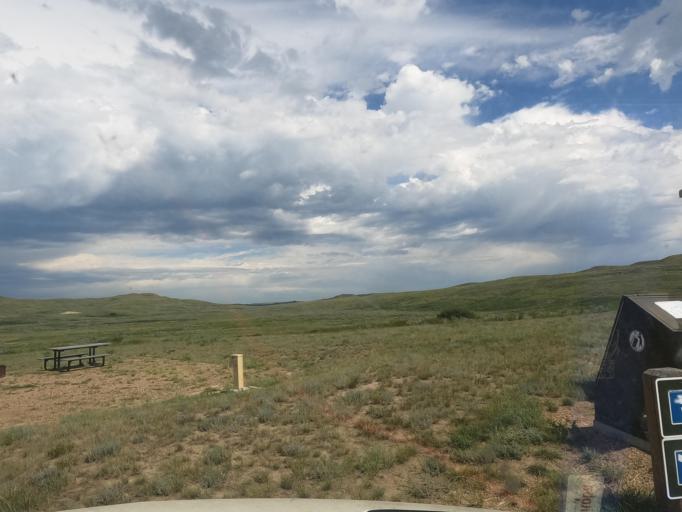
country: CA
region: Saskatchewan
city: Assiniboia
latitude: 49.0709
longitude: -106.5278
